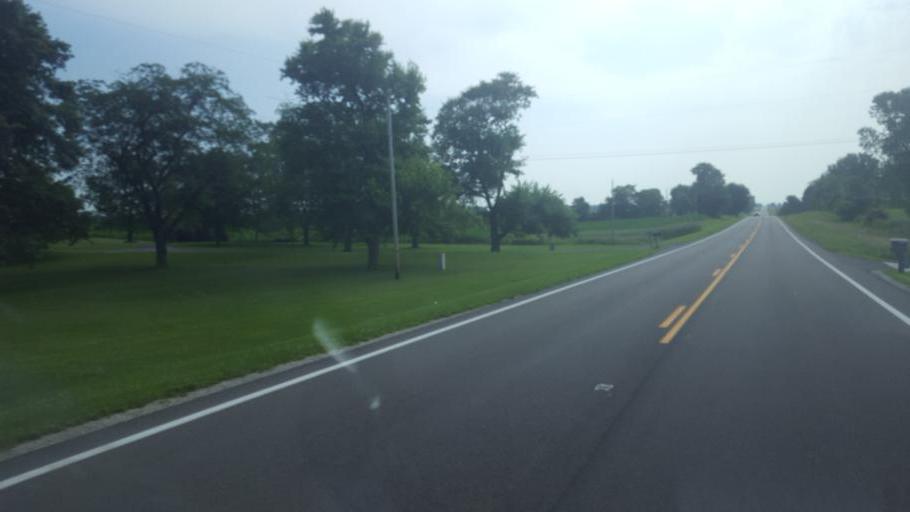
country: US
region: Ohio
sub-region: Hardin County
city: Kenton
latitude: 40.6442
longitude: -83.5647
